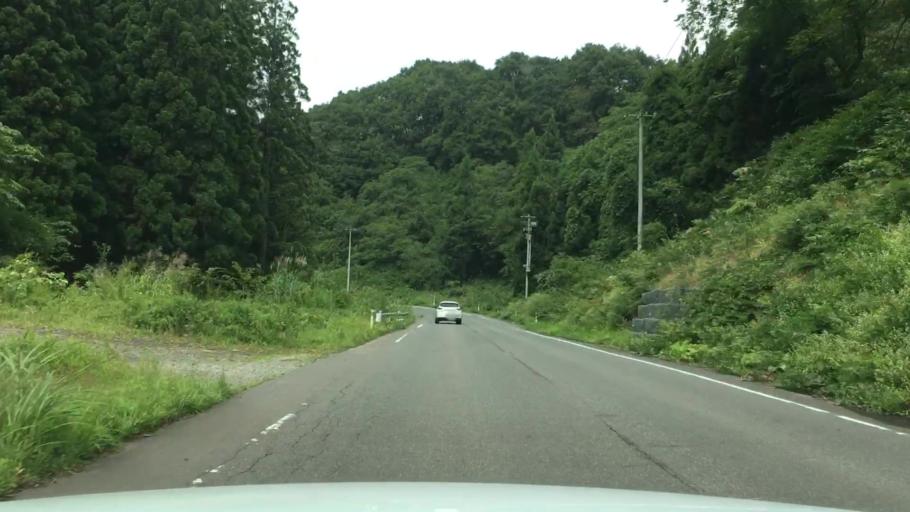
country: JP
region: Aomori
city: Shimokizukuri
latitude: 40.7324
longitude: 140.2516
